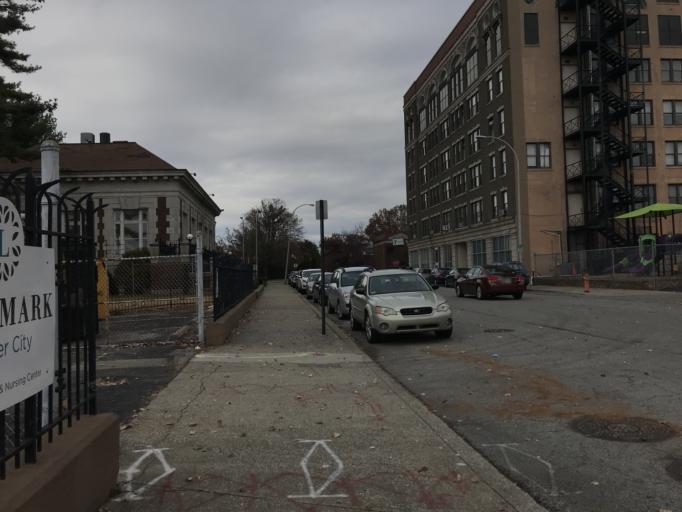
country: US
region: Kentucky
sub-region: Jefferson County
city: Louisville
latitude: 38.2494
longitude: -85.7680
